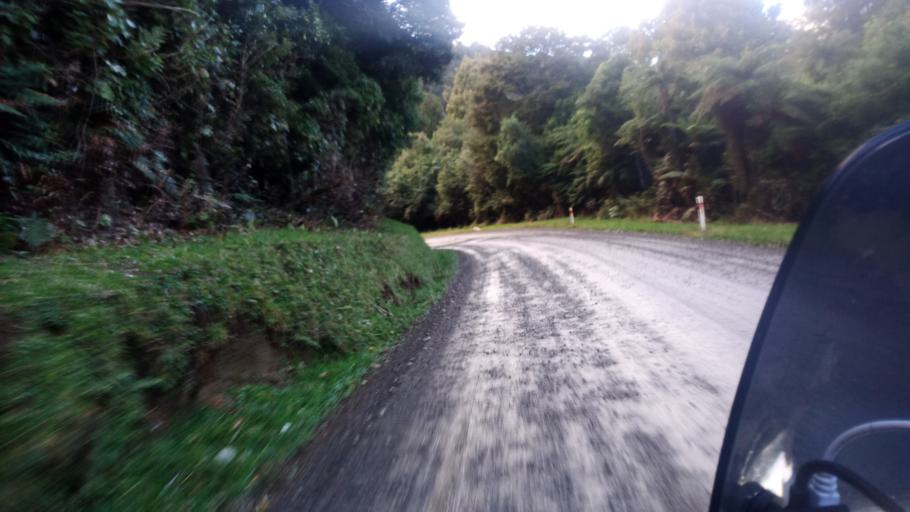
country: NZ
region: Hawke's Bay
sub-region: Wairoa District
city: Wairoa
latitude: -38.7449
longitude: 177.1154
